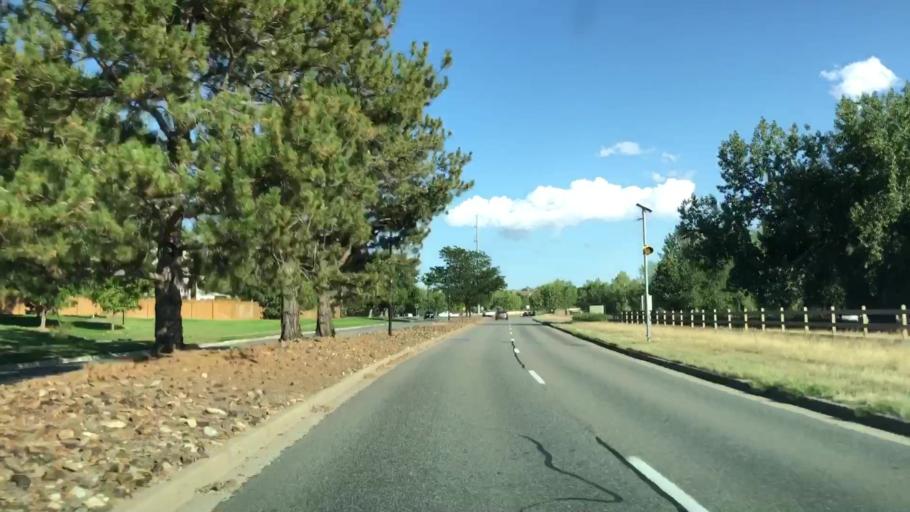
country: US
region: Colorado
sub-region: Arapahoe County
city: Dove Valley
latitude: 39.6116
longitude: -104.7947
